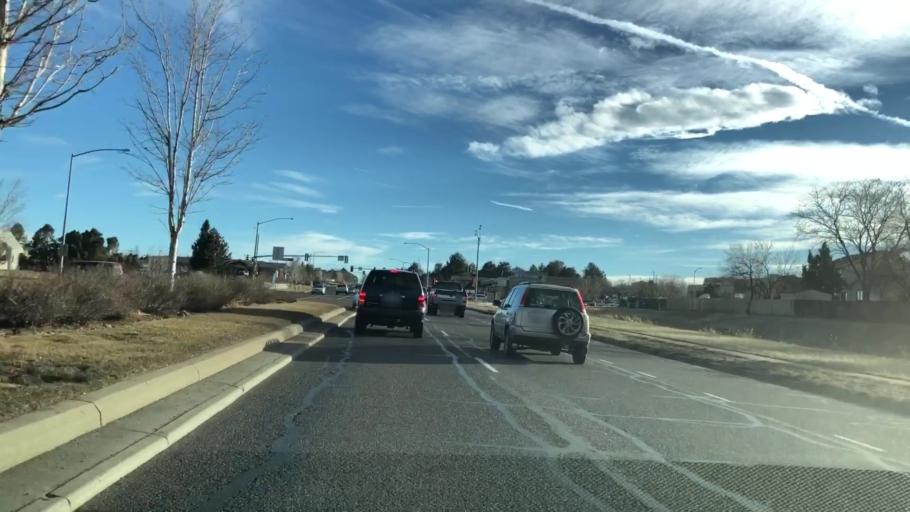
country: US
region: Colorado
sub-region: Adams County
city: Aurora
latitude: 39.6981
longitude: -104.7912
